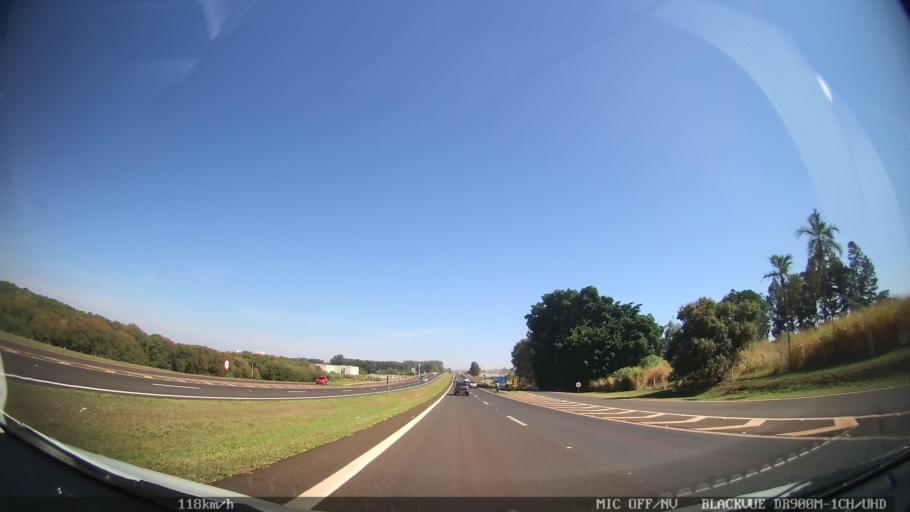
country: BR
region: Sao Paulo
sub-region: Ribeirao Preto
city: Ribeirao Preto
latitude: -21.1152
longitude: -47.8246
